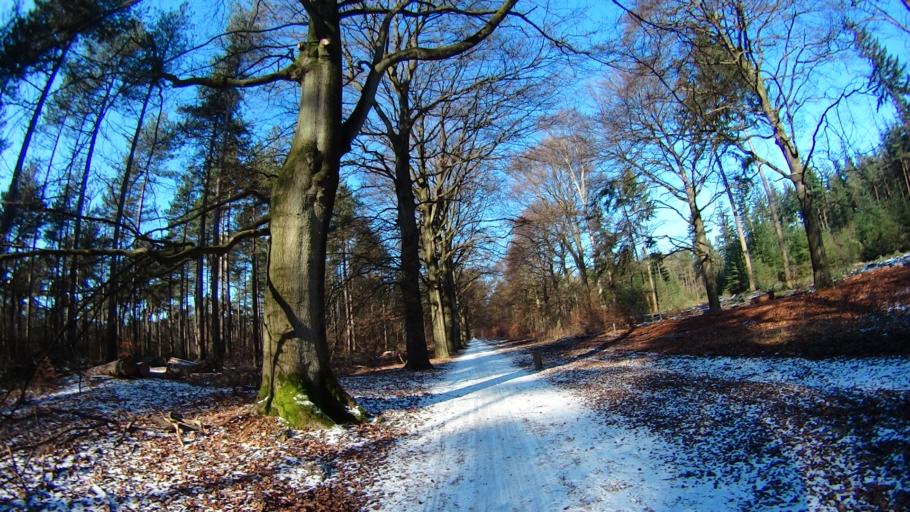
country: NL
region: North Holland
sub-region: Gemeente Hilversum
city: Hilversum
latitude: 52.1887
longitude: 5.2161
